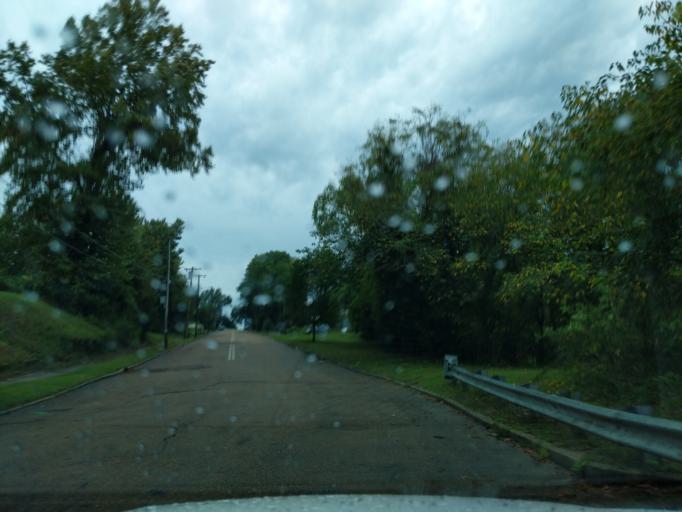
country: US
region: Mississippi
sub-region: Warren County
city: Vicksburg
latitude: 32.3571
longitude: -90.8774
